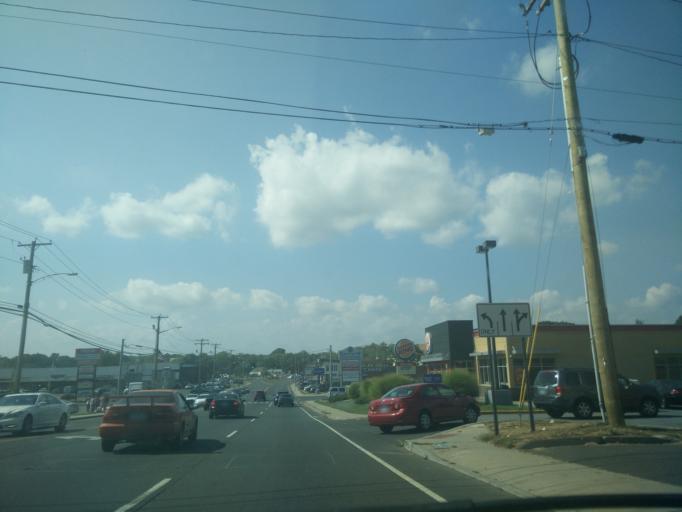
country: US
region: Connecticut
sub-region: Fairfield County
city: Bridgeport
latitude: 41.2015
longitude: -73.1855
